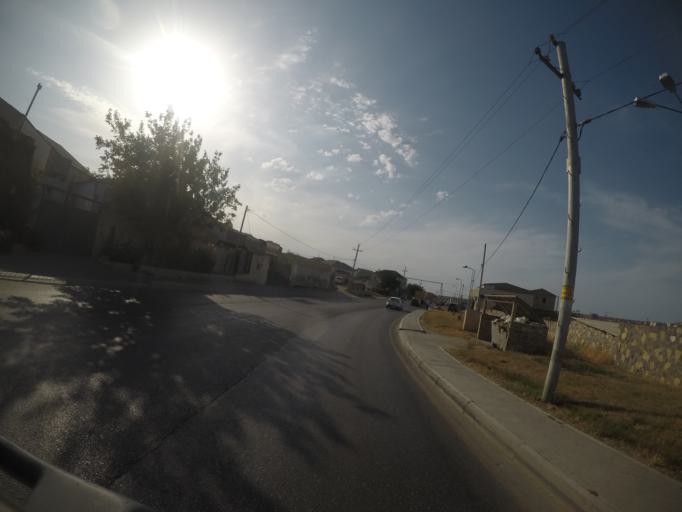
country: AZ
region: Baki
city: Binagadi
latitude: 40.4740
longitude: 49.8343
